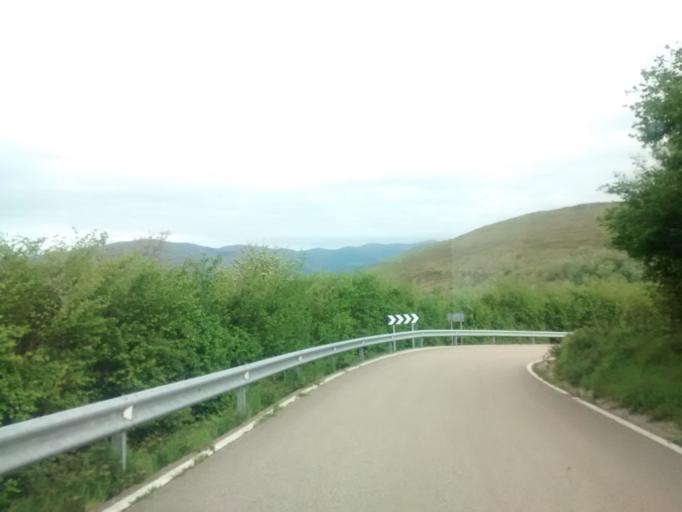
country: ES
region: Cantabria
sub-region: Provincia de Cantabria
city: San Vicente de la Barquera
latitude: 43.2566
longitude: -4.4406
